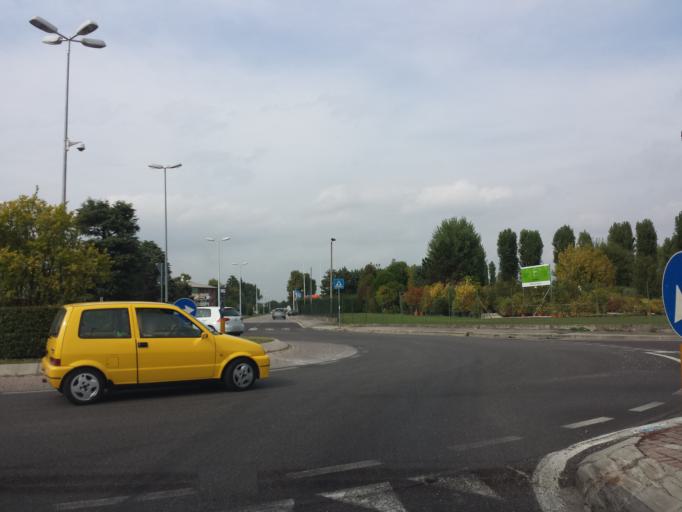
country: IT
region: Veneto
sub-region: Provincia di Padova
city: Padova
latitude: 45.4301
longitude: 11.8990
